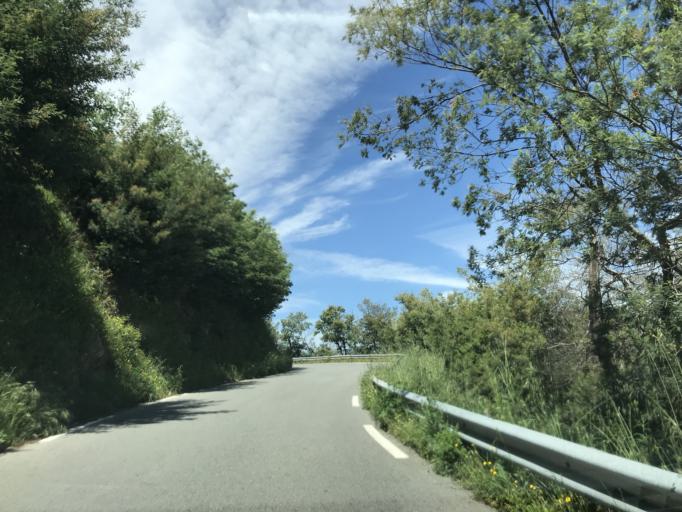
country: FR
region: Provence-Alpes-Cote d'Azur
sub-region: Departement du Var
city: Tanneron
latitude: 43.5887
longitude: 6.8801
